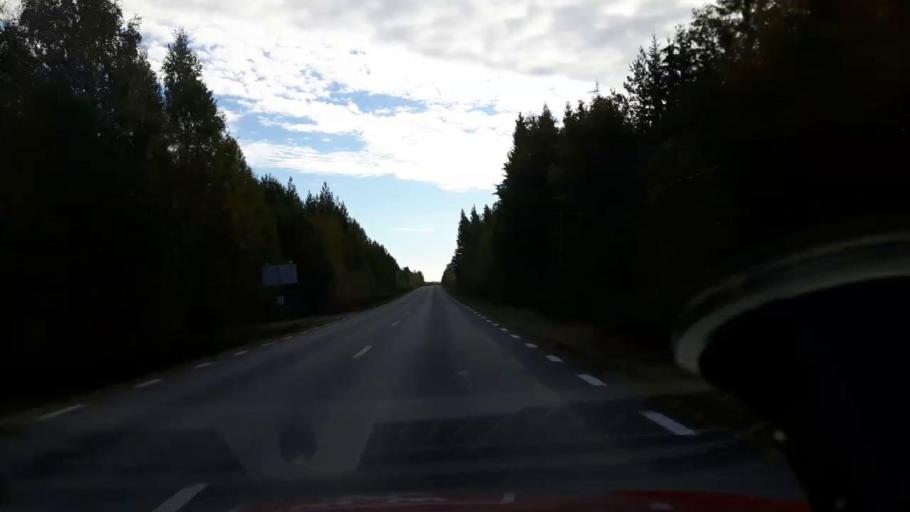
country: SE
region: Gaevleborg
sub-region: Ljusdals Kommun
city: Farila
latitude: 61.9915
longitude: 15.2634
